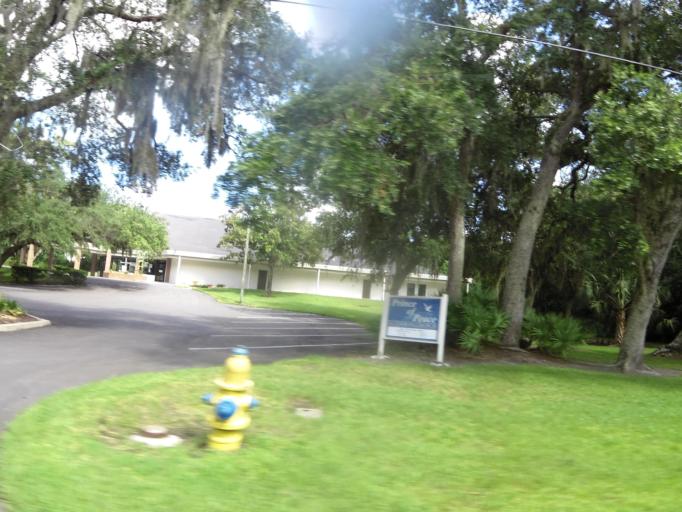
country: US
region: Florida
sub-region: Nassau County
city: Fernandina Beach
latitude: 30.6674
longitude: -81.4355
